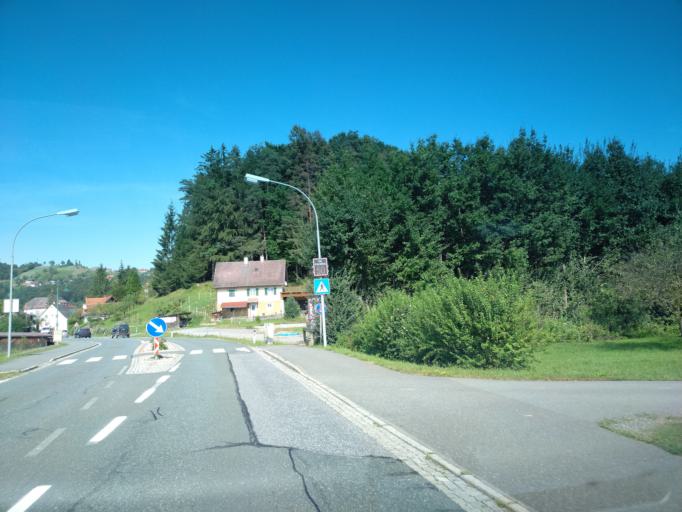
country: AT
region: Styria
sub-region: Politischer Bezirk Leibnitz
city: Grossklein
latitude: 46.7335
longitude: 15.4391
